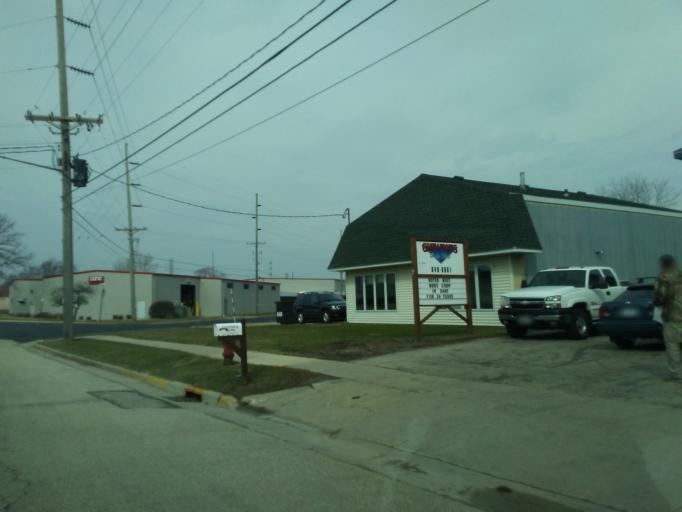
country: US
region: Wisconsin
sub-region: Columbia County
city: Lodi
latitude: 43.2505
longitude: -89.4976
